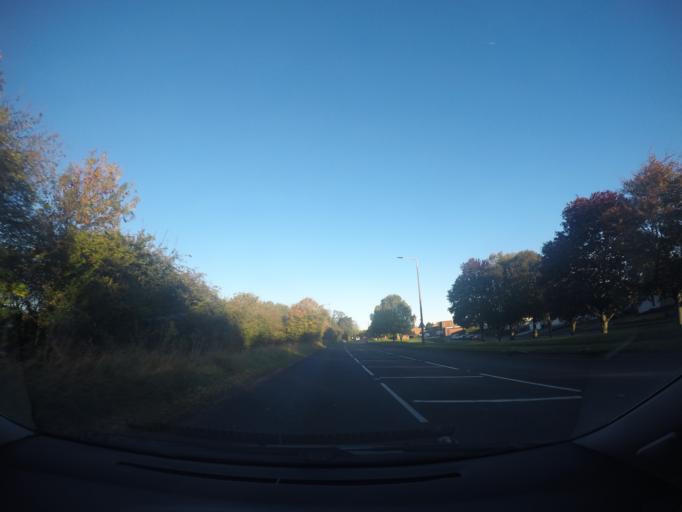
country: GB
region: England
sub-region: City of York
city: Skelton
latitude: 53.9816
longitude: -1.1166
